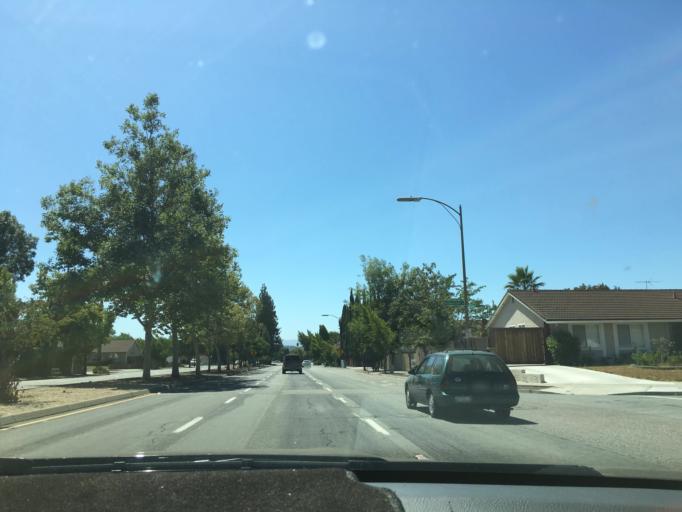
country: US
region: California
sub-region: Santa Clara County
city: Seven Trees
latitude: 37.2370
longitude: -121.8131
